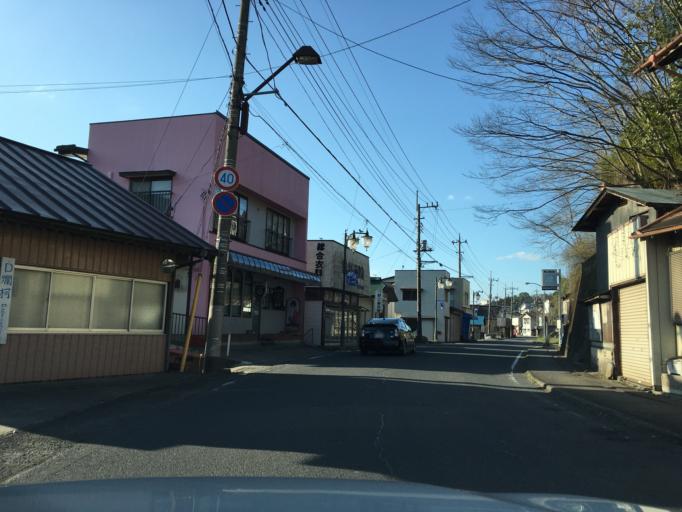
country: JP
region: Ibaraki
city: Daigo
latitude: 36.7721
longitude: 140.3510
